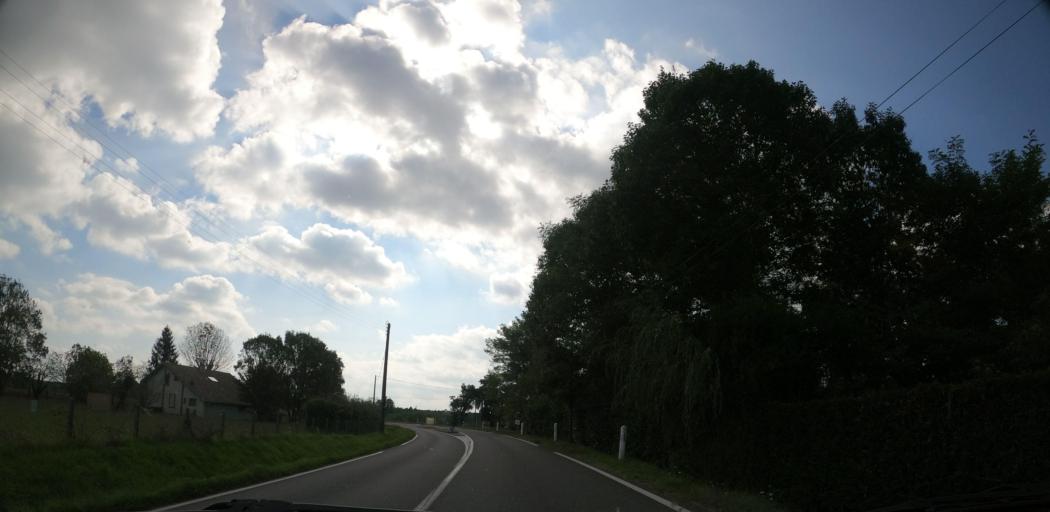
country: FR
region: Aquitaine
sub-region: Departement des Landes
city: Tosse
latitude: 43.7184
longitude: -1.3465
